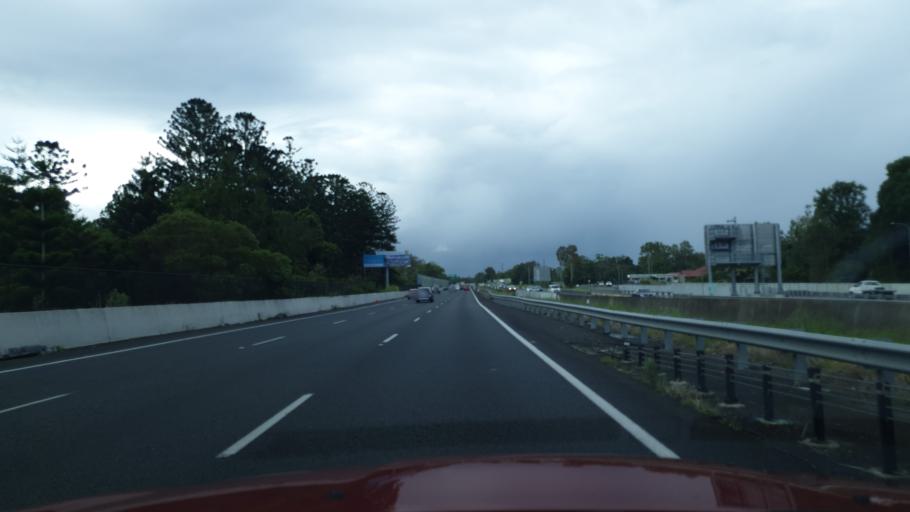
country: AU
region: Queensland
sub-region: Moreton Bay
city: Burpengary
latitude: -27.1529
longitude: 152.9776
